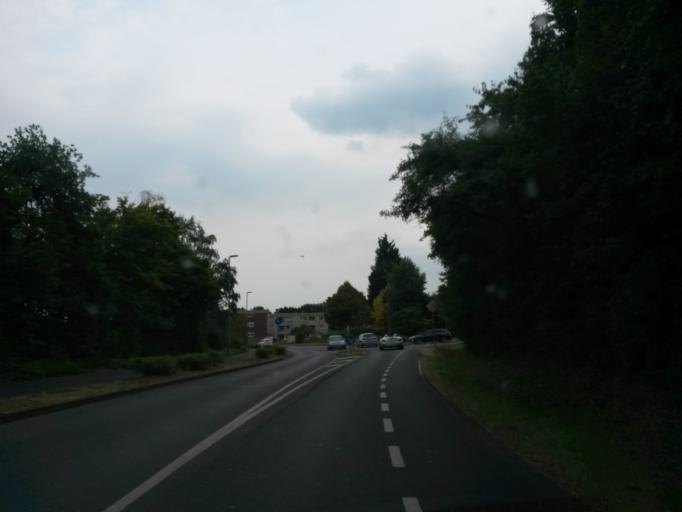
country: DE
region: North Rhine-Westphalia
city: Sankt Augustin
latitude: 50.7630
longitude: 7.1801
